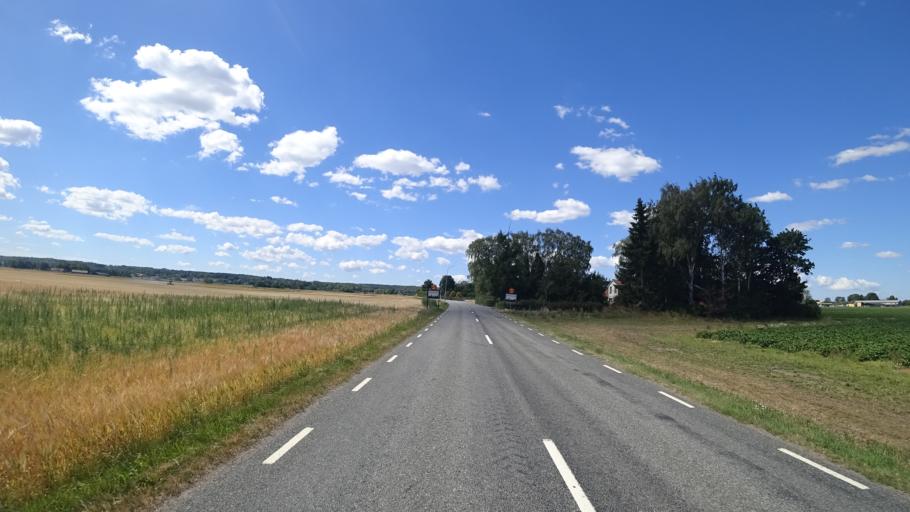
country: SE
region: Skane
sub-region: Kristianstads Kommun
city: Onnestad
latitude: 56.0598
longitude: 14.0376
